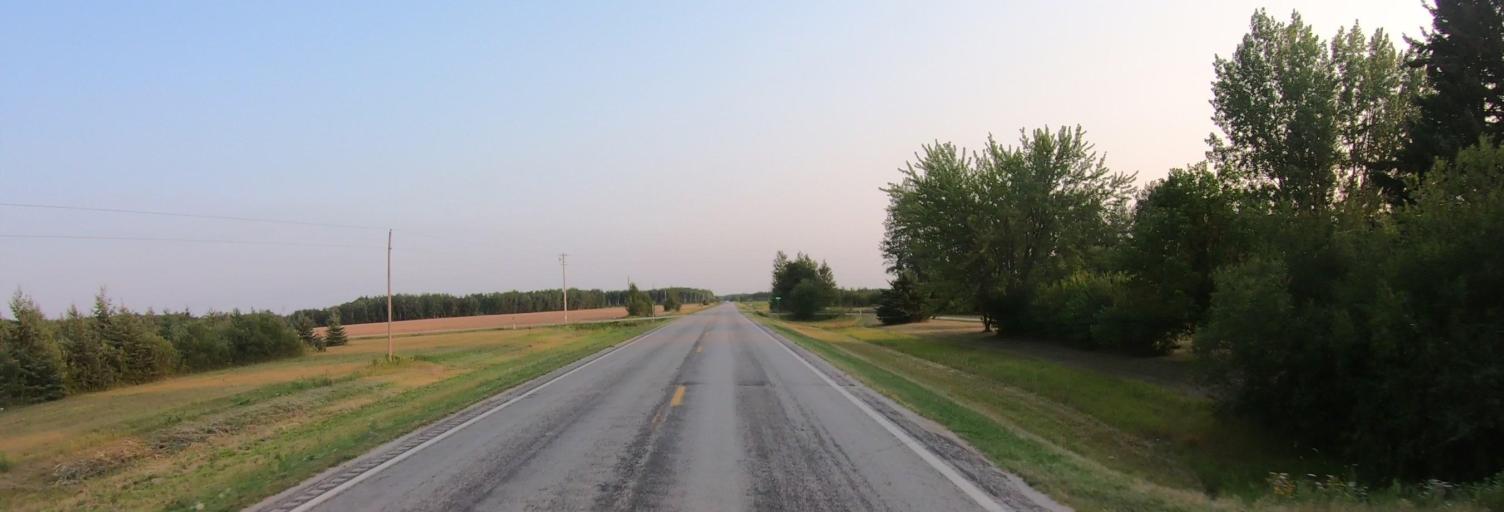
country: US
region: Minnesota
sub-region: Roseau County
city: Warroad
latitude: 48.7719
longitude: -95.3306
